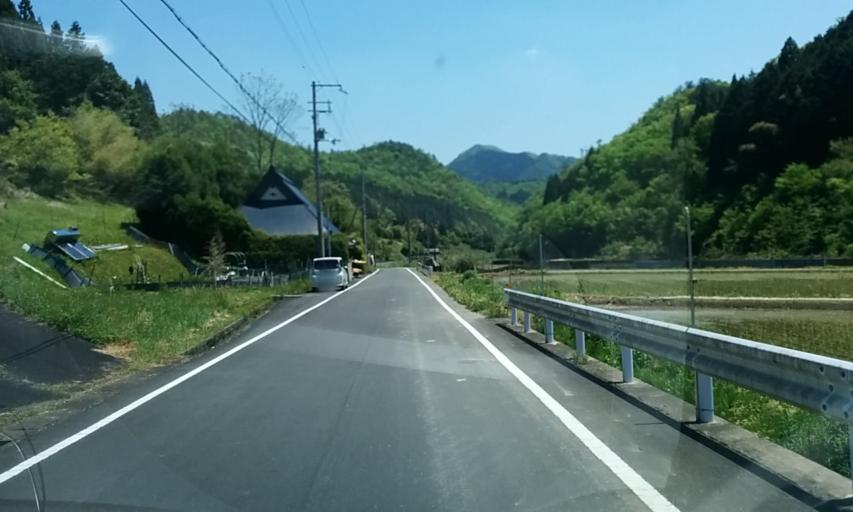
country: JP
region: Kyoto
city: Ayabe
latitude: 35.2241
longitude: 135.2886
